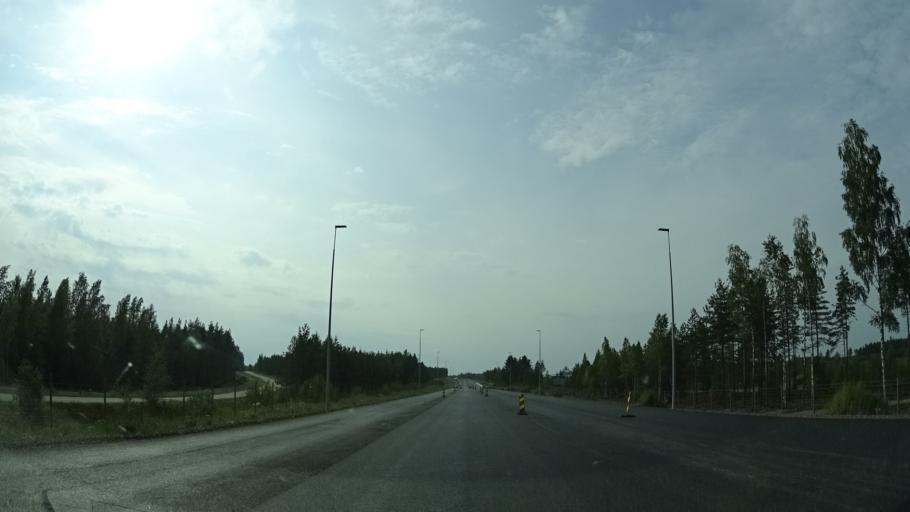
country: FI
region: South Karelia
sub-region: Lappeenranta
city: Luumaeki
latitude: 60.9287
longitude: 27.6084
